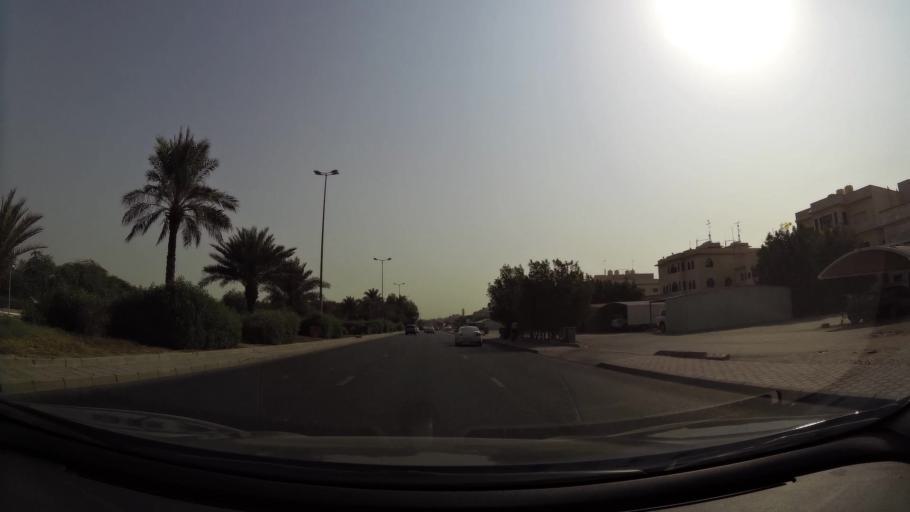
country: KW
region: Al Asimah
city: Ar Rabiyah
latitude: 29.2745
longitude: 47.8755
